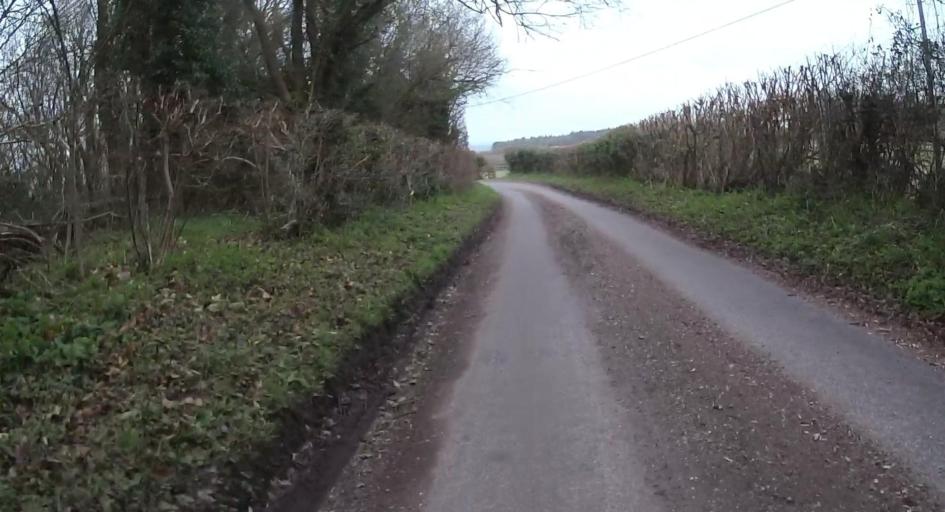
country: GB
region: England
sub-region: Hampshire
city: Four Marks
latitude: 51.0914
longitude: -1.1001
